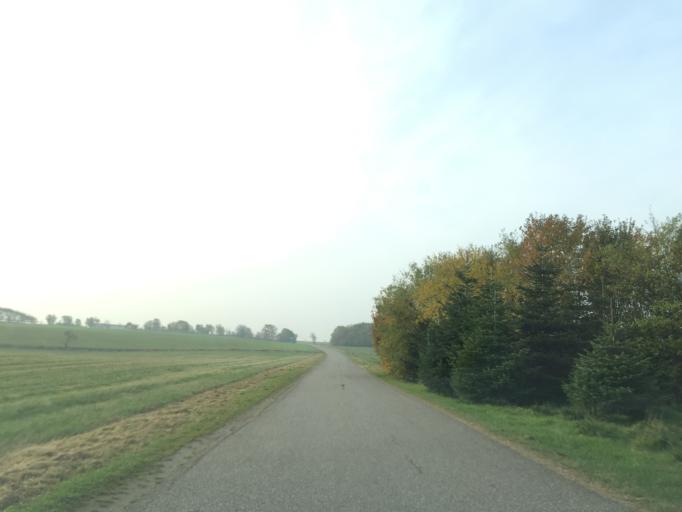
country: DK
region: Central Jutland
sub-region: Silkeborg Kommune
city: Svejbaek
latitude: 56.2329
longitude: 9.6473
